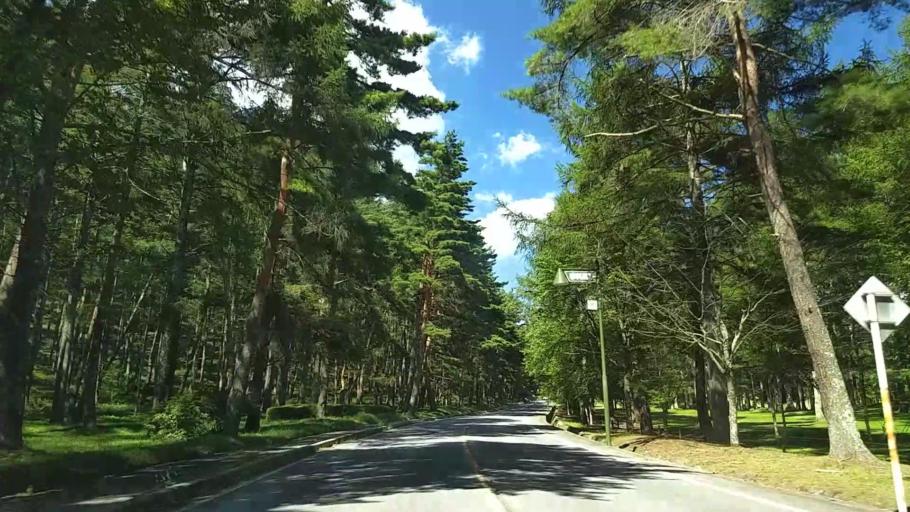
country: JP
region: Nagano
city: Chino
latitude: 36.0450
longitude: 138.2482
